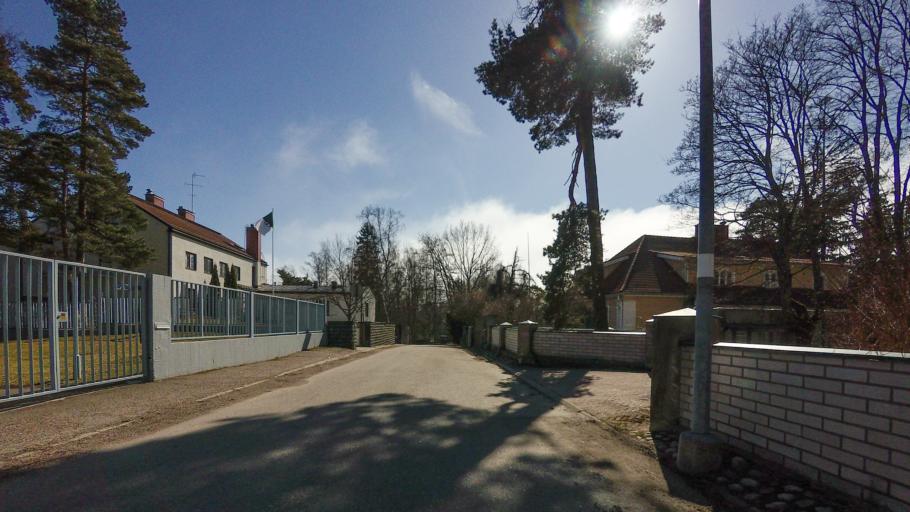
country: FI
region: Uusimaa
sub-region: Helsinki
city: Helsinki
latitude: 60.1851
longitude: 25.0165
